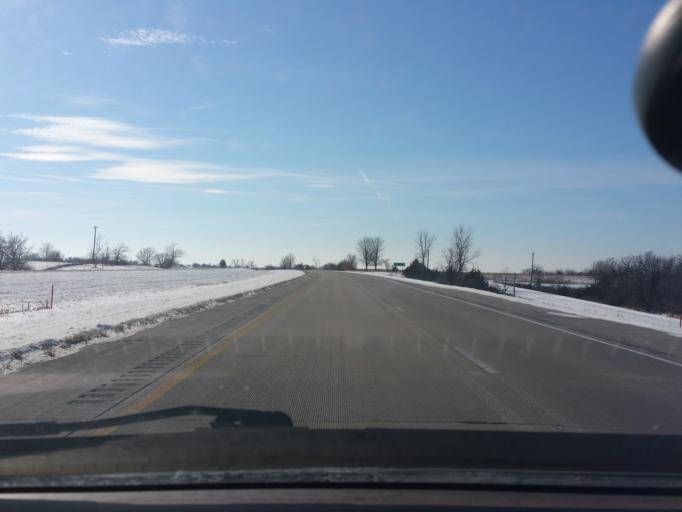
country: US
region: Iowa
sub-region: Decatur County
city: Leon
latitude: 40.7986
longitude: -93.8333
